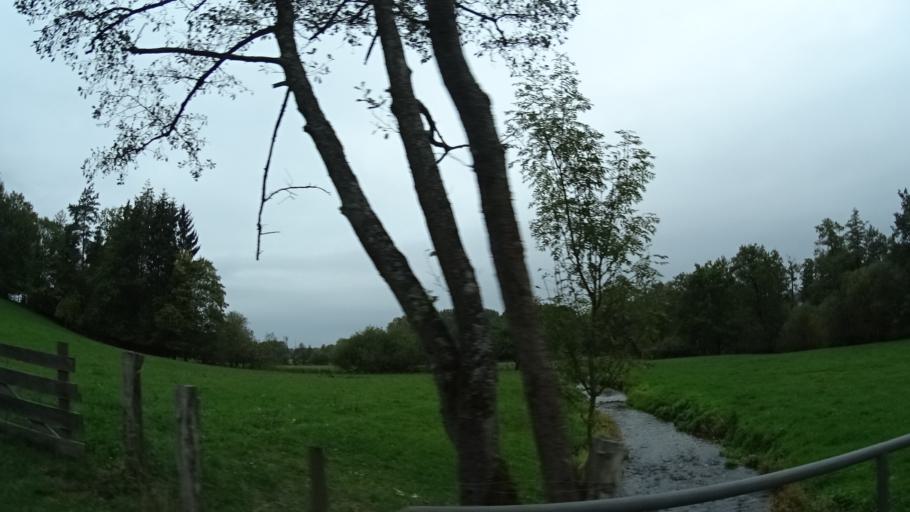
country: DE
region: Hesse
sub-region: Regierungsbezirk Kassel
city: Eichenzell
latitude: 50.4721
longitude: 9.7515
